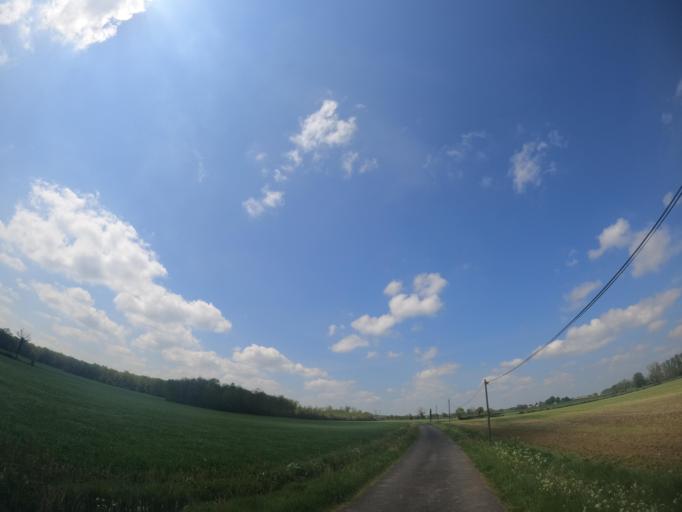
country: FR
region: Poitou-Charentes
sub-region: Departement des Deux-Sevres
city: Saint-Varent
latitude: 46.8520
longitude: -0.2304
